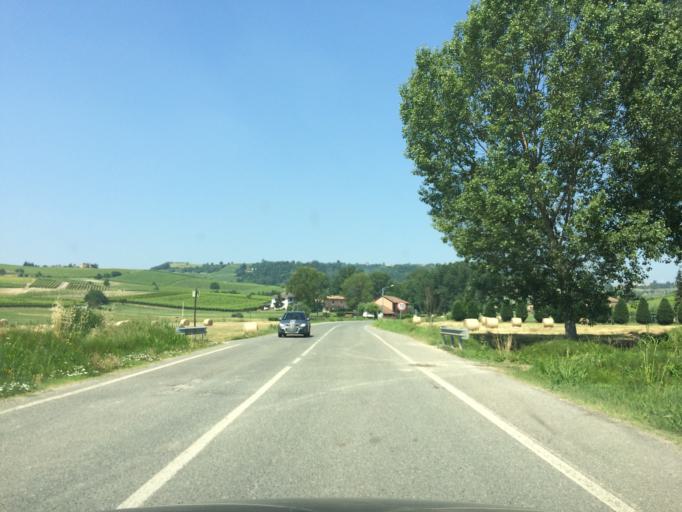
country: IT
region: Piedmont
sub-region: Provincia di Asti
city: Calosso
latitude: 44.7744
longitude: 8.2184
